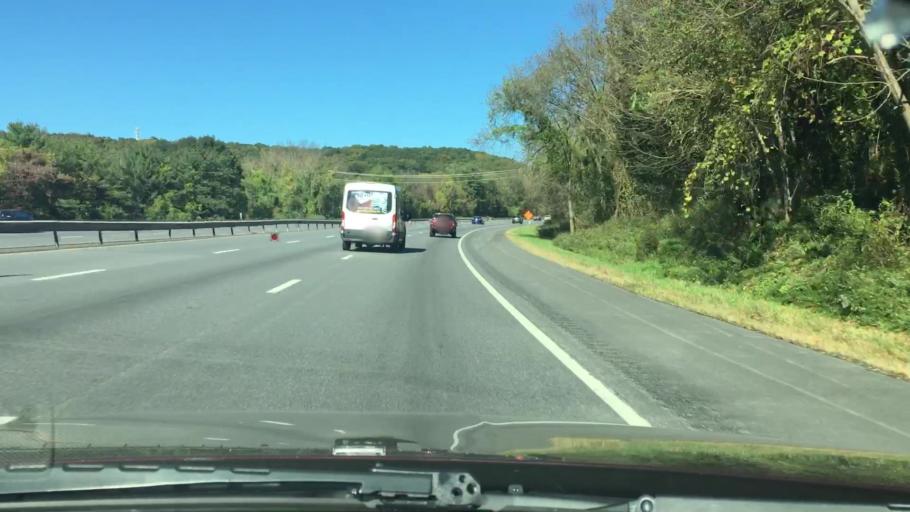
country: US
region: New York
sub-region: Westchester County
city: Heritage Hills
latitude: 41.3415
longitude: -73.6556
